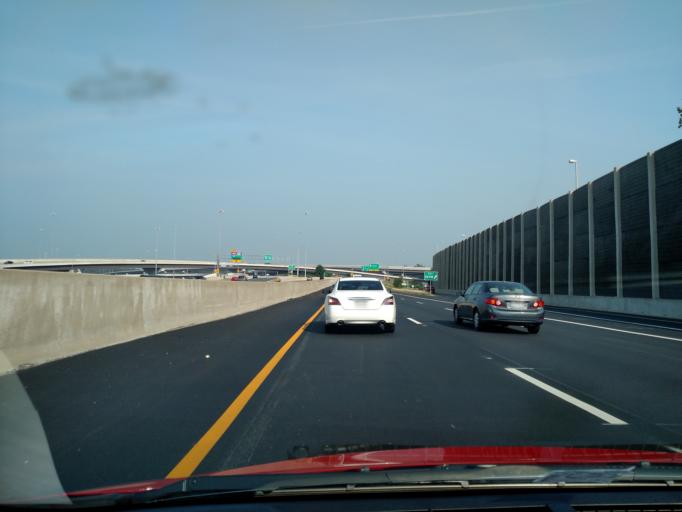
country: US
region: Virginia
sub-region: Fairfax County
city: Springfield
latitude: 38.7927
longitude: -77.1815
